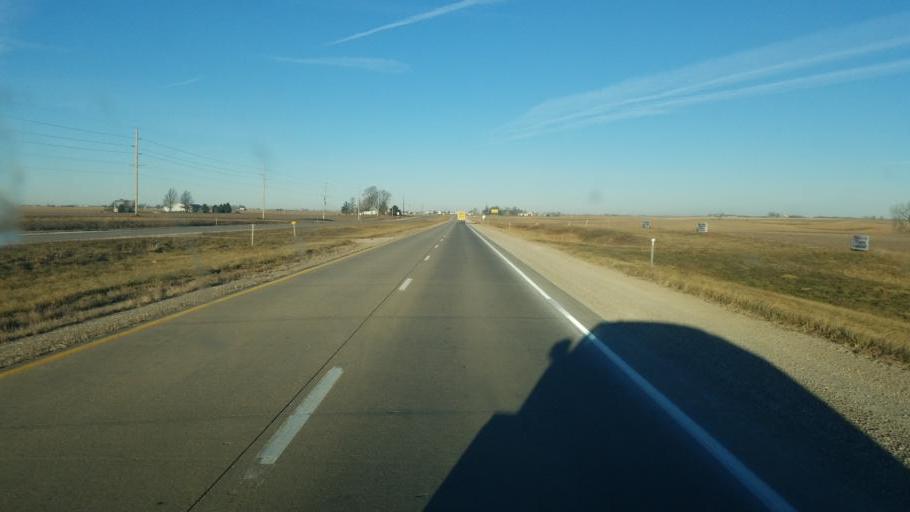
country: US
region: Iowa
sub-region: Marion County
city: Pella
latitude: 41.3609
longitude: -92.7777
